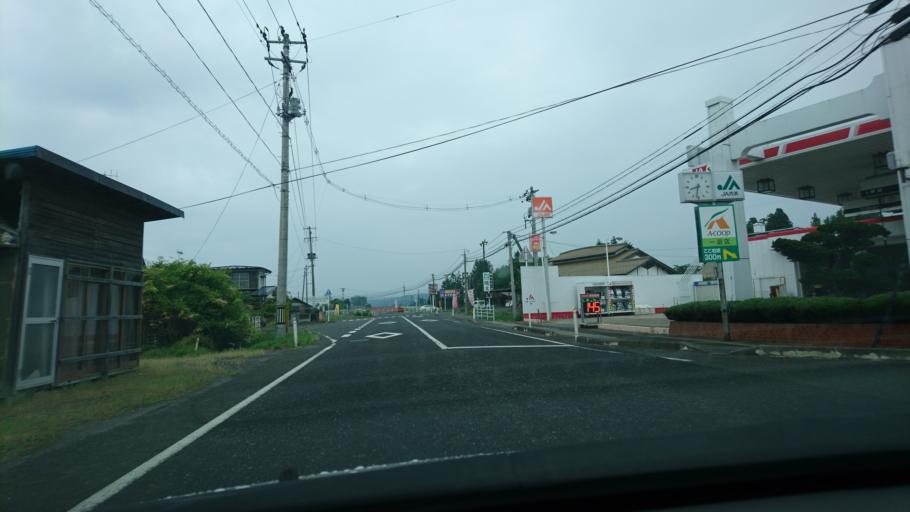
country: JP
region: Miyagi
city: Furukawa
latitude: 38.7389
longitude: 140.9492
